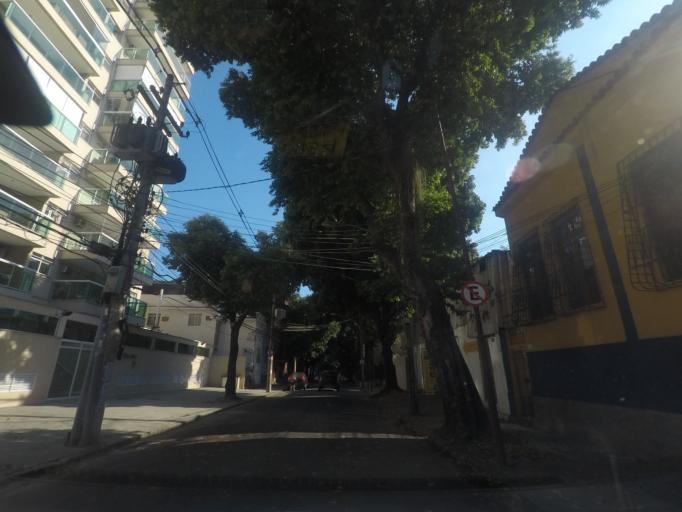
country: BR
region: Rio de Janeiro
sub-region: Rio De Janeiro
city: Rio de Janeiro
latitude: -22.9120
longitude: -43.2167
